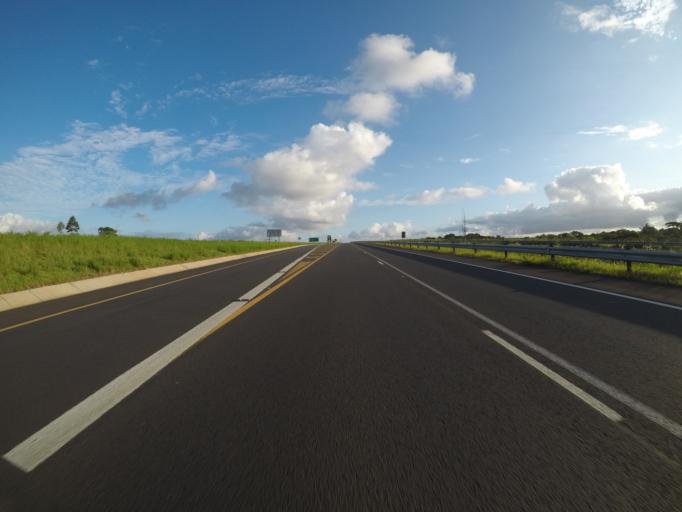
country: ZA
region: KwaZulu-Natal
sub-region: uThungulu District Municipality
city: KwaMbonambi
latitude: -28.5087
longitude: 32.1377
